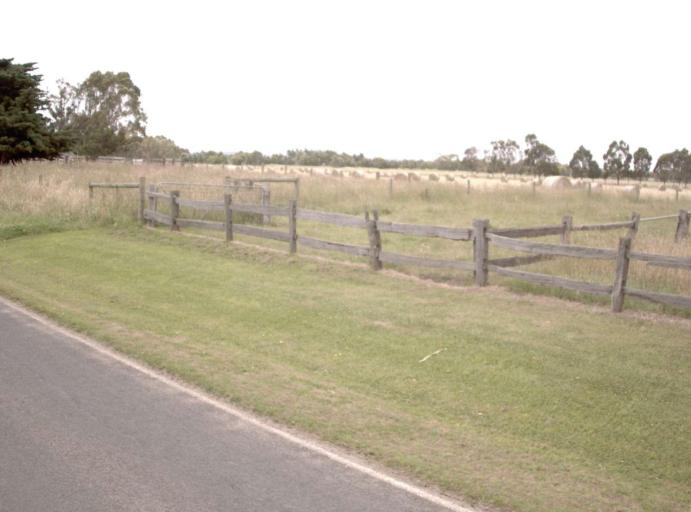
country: AU
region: Victoria
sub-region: Latrobe
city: Traralgon
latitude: -38.5154
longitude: 146.6619
